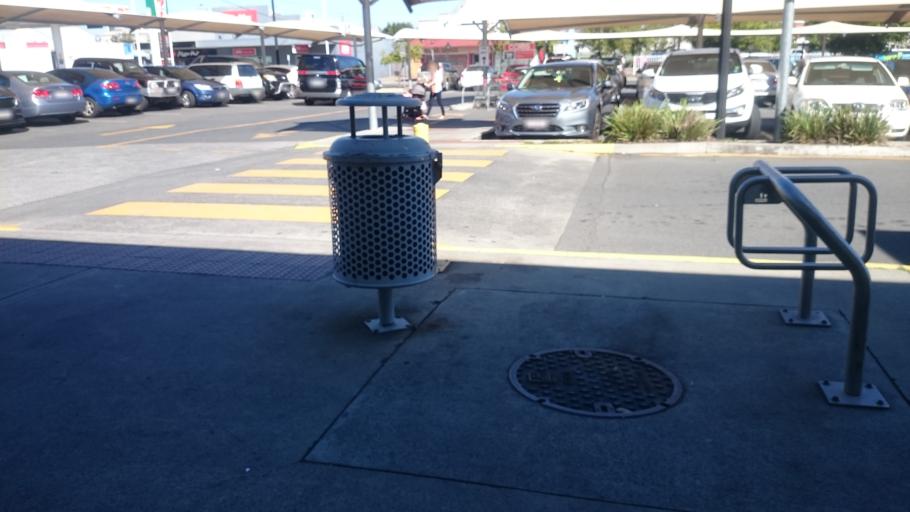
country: AU
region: Queensland
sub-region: Brisbane
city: Wynnum
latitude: -27.4452
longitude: 153.1719
